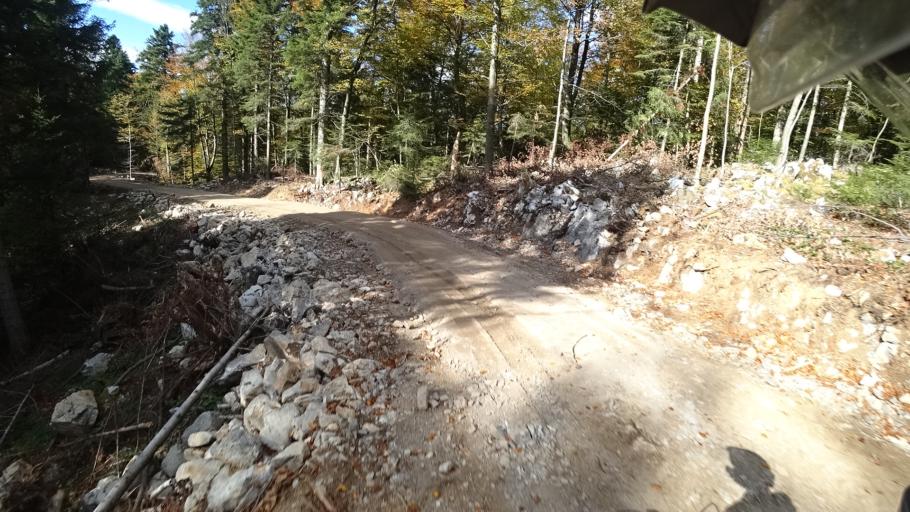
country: HR
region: Karlovacka
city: Plaski
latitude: 45.0599
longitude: 15.3524
